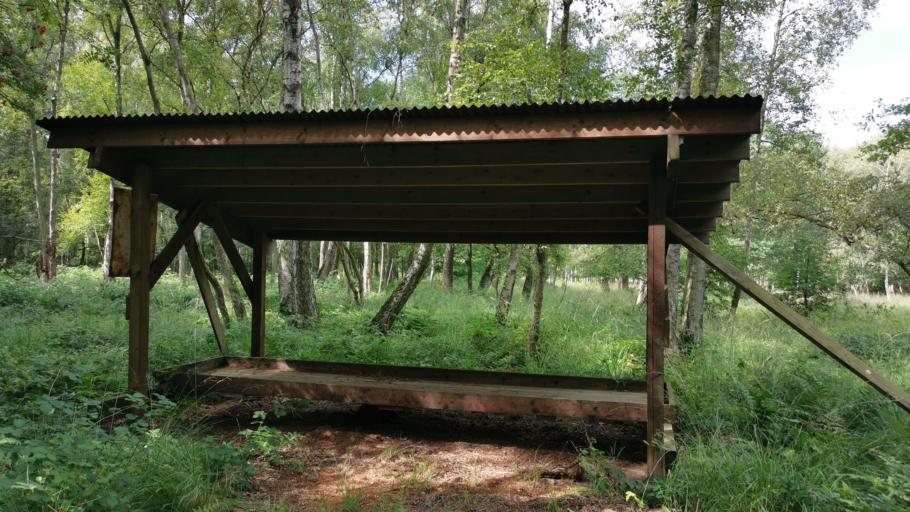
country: DE
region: Schleswig-Holstein
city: Gudow
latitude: 53.5791
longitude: 10.7655
